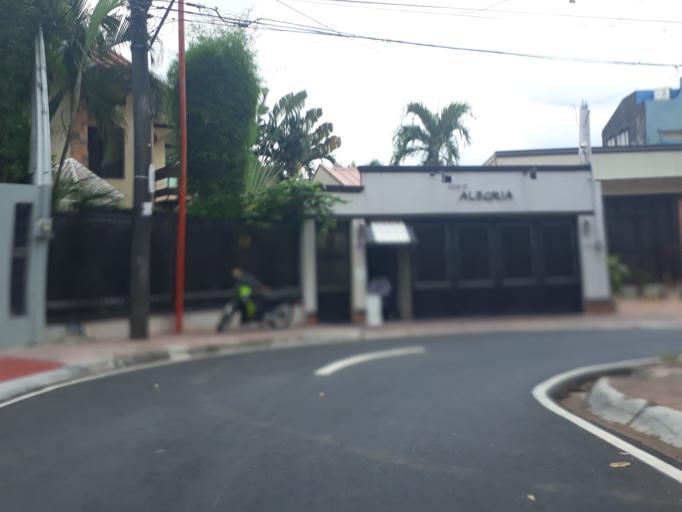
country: PH
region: Calabarzon
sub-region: Province of Rizal
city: Antipolo
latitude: 14.6438
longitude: 121.1184
